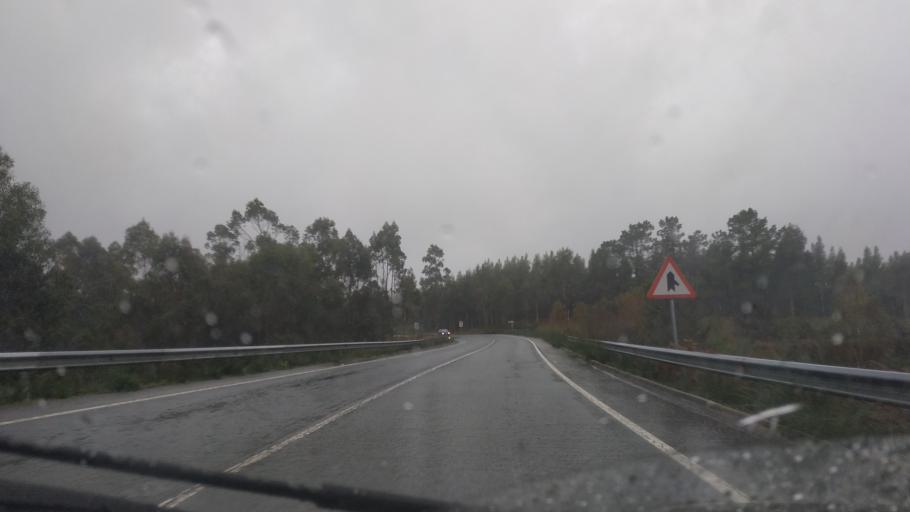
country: ES
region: Galicia
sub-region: Provincia da Coruna
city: Cerceda
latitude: 43.1685
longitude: -8.5104
